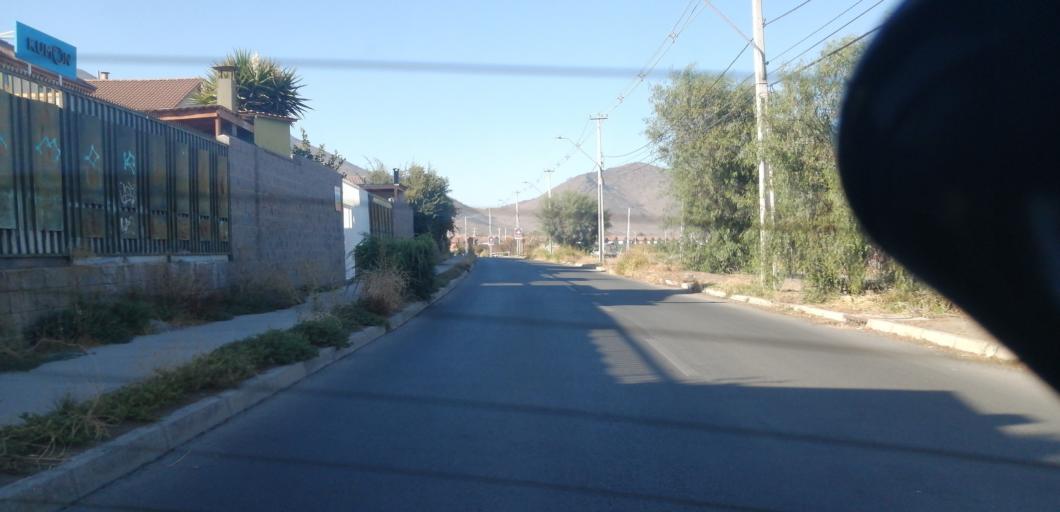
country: CL
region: Santiago Metropolitan
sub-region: Provincia de Santiago
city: Lo Prado
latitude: -33.4569
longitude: -70.8555
